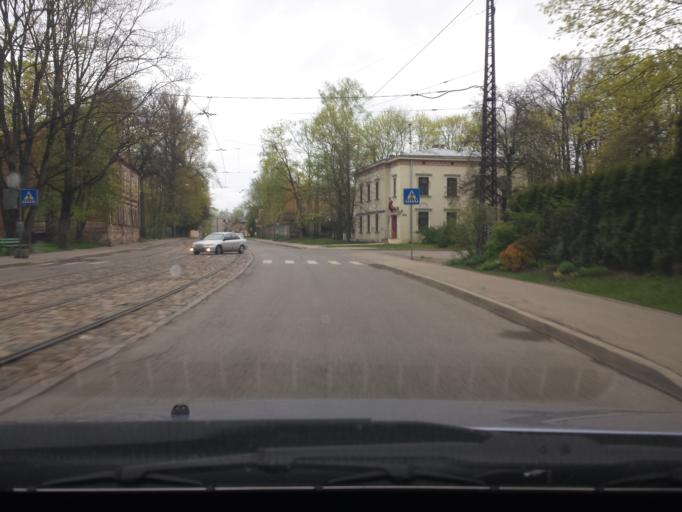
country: LV
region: Riga
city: Riga
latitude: 56.9563
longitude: 24.0628
